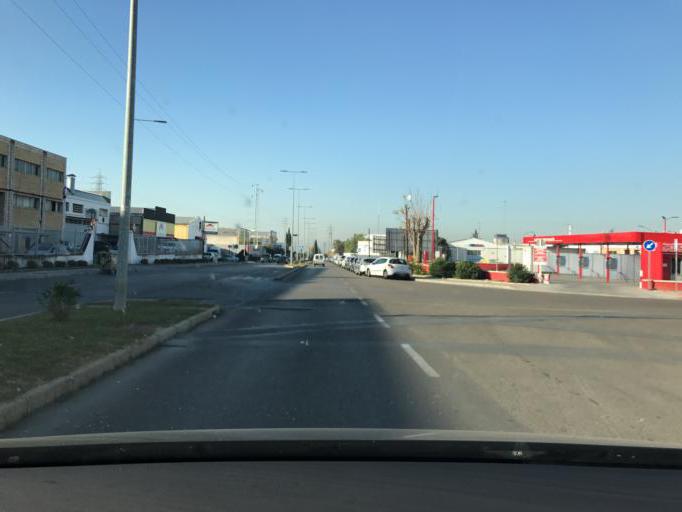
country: ES
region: Andalusia
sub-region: Provincia de Granada
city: Peligros
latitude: 37.2237
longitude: -3.6263
